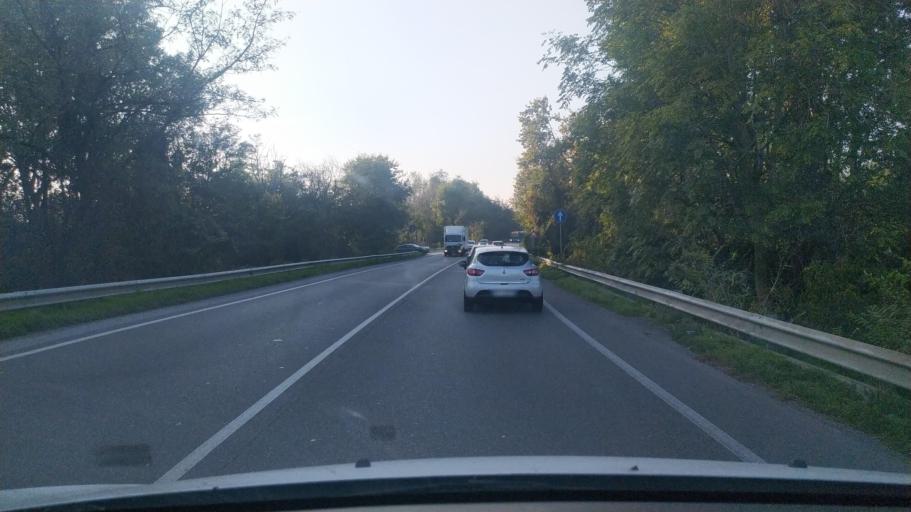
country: IT
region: Lombardy
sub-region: Provincia di Lodi
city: Zelo Buon Persico
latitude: 45.4038
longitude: 9.4526
